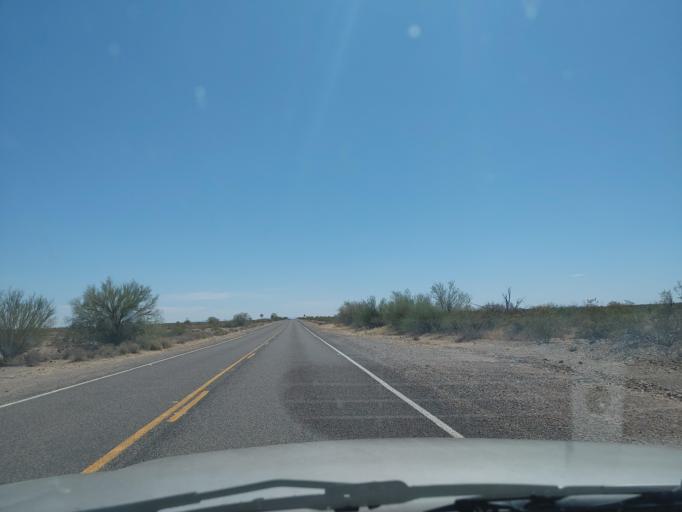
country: US
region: Arizona
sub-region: Maricopa County
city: Gila Bend
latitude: 32.8907
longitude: -113.2414
